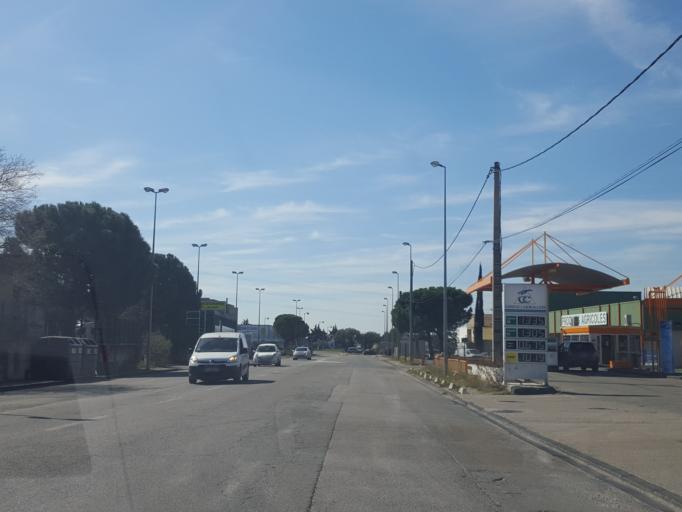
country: FR
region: Provence-Alpes-Cote d'Azur
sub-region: Departement du Vaucluse
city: Carpentras
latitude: 44.0354
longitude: 5.0397
